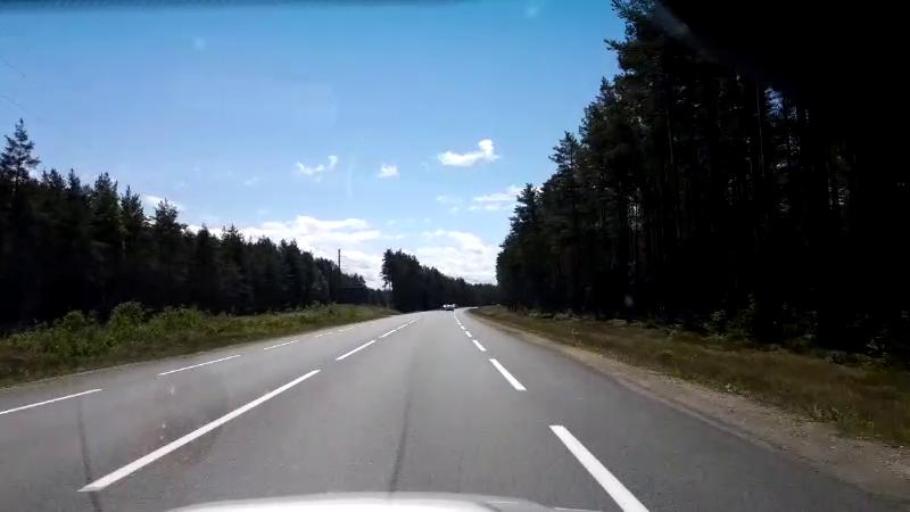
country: LV
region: Saulkrastu
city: Saulkrasti
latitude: 57.2368
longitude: 24.4272
